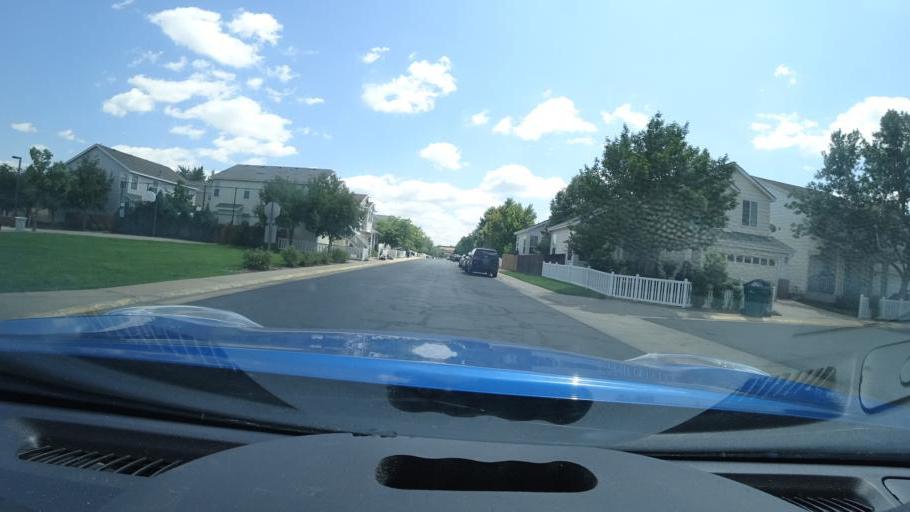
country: US
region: Colorado
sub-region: Arapahoe County
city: Glendale
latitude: 39.6940
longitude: -104.8808
